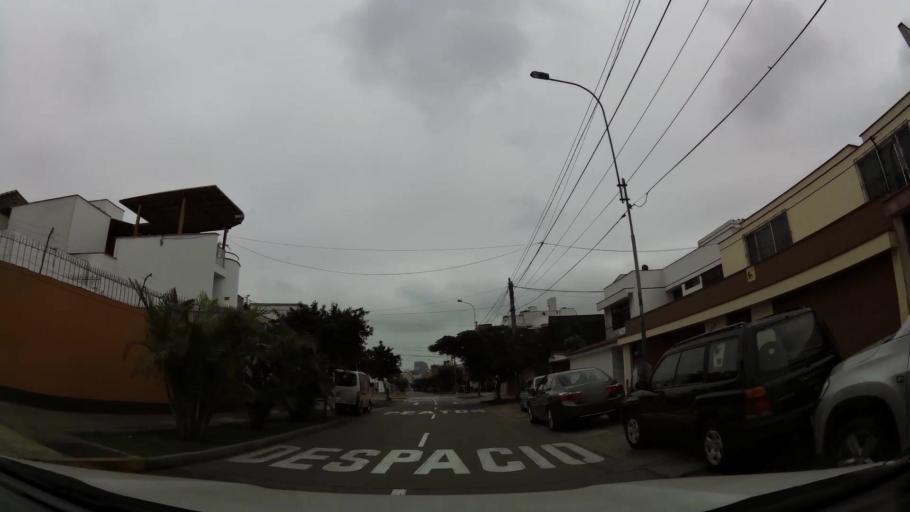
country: PE
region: Lima
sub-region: Lima
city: San Luis
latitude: -12.0951
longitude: -77.0053
